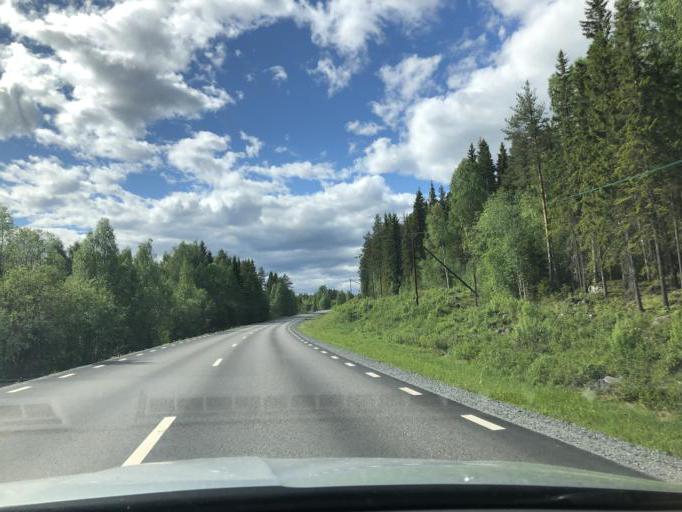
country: SE
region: Norrbotten
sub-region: Alvsbyns Kommun
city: AElvsbyn
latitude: 65.6783
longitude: 20.7529
